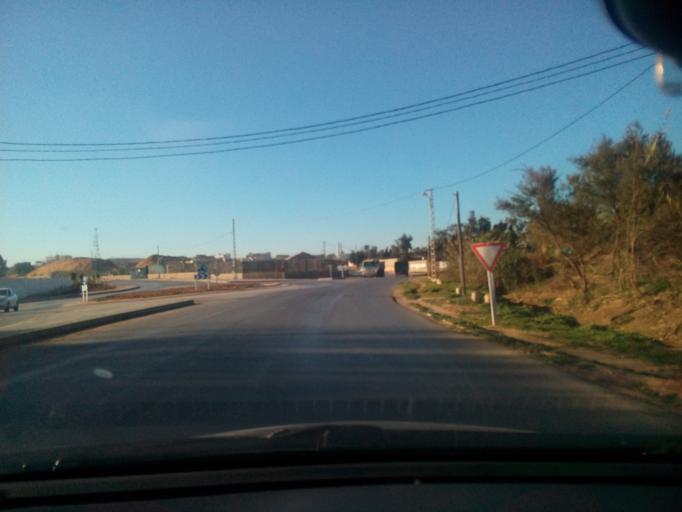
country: DZ
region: Mostaganem
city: Mostaganem
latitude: 35.9202
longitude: 0.1234
